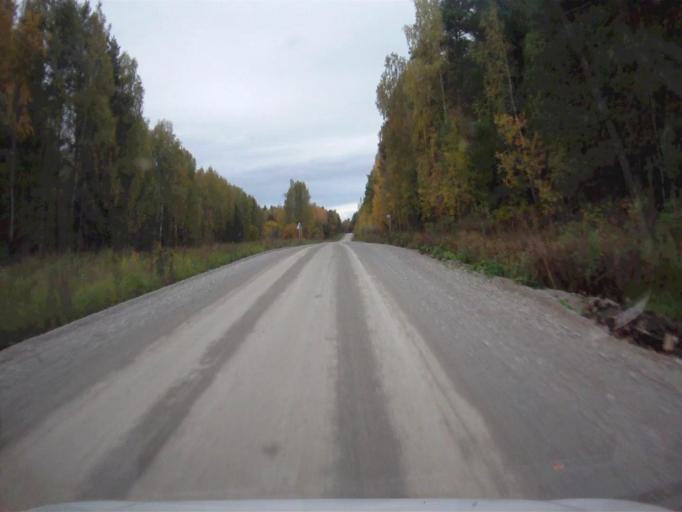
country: RU
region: Chelyabinsk
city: Nyazepetrovsk
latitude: 56.0798
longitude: 59.4234
